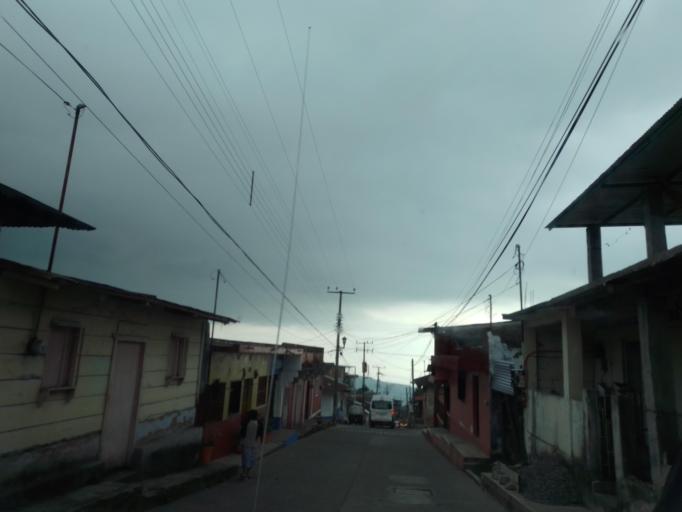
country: MX
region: Chiapas
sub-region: Union Juarez
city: Santo Domingo
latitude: 15.0618
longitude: -92.0814
